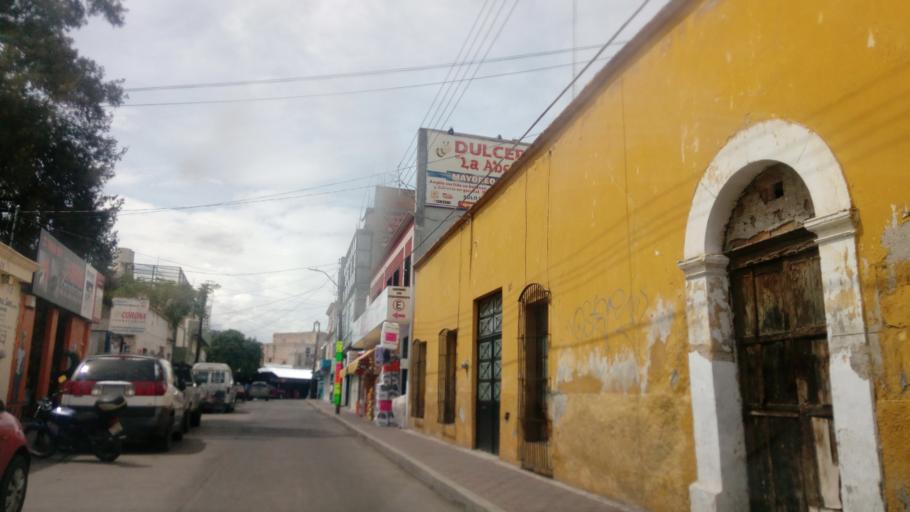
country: MX
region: Durango
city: Victoria de Durango
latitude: 24.0217
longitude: -104.6652
